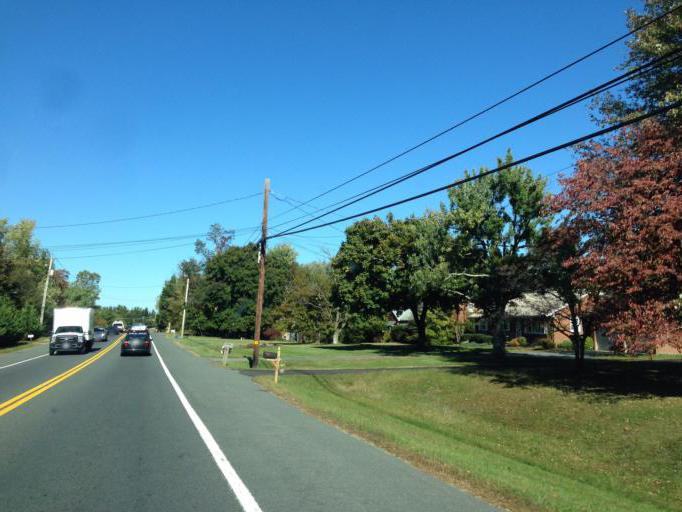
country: US
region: Maryland
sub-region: Montgomery County
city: Damascus
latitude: 39.2574
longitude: -77.2253
